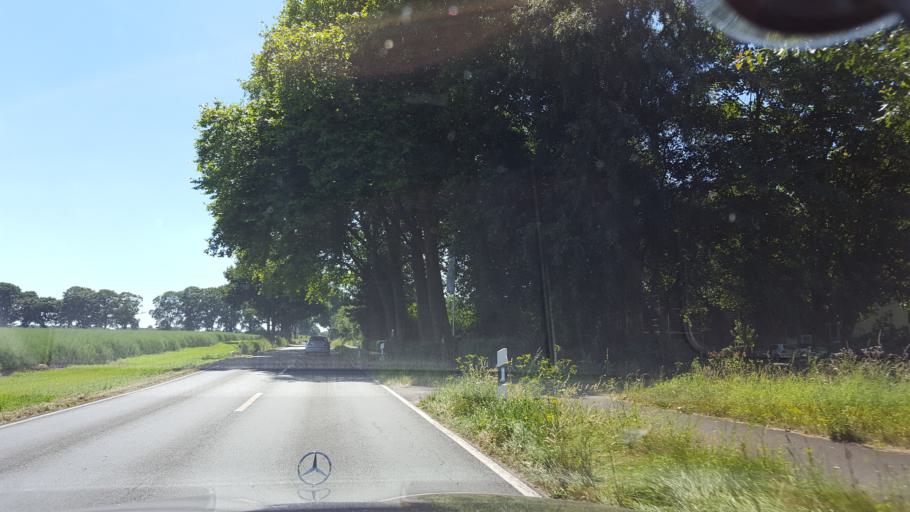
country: DE
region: North Rhine-Westphalia
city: Herten
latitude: 51.6341
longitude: 7.1562
